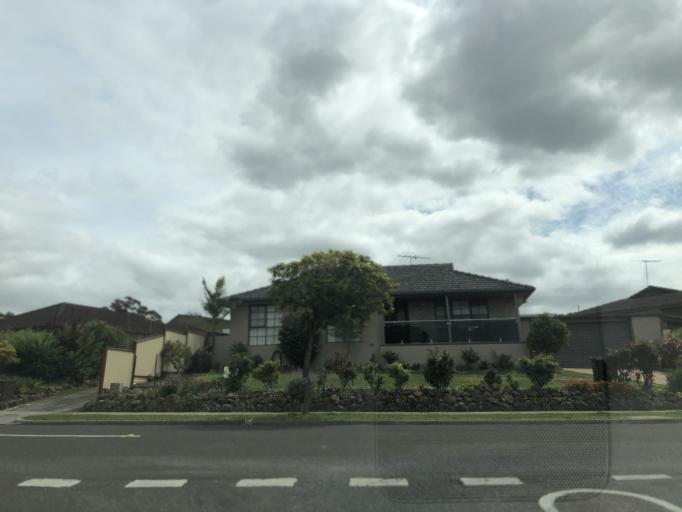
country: AU
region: Victoria
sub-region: Greater Dandenong
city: Dandenong North
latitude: -37.9540
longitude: 145.2066
